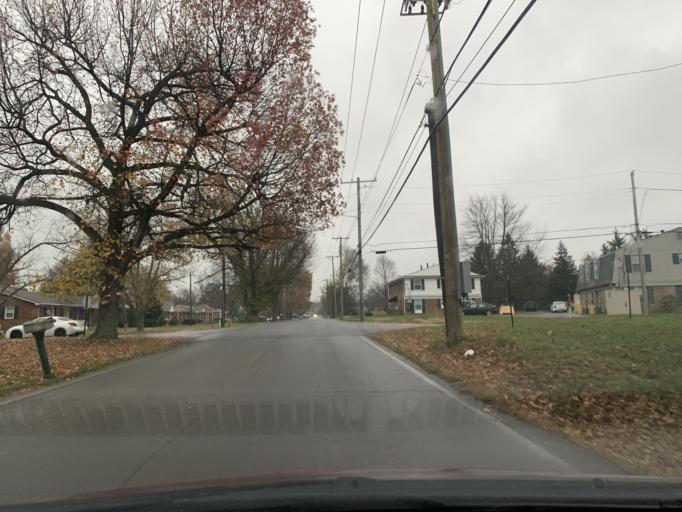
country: US
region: Kentucky
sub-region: Jefferson County
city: Buechel
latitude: 38.1979
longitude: -85.6332
